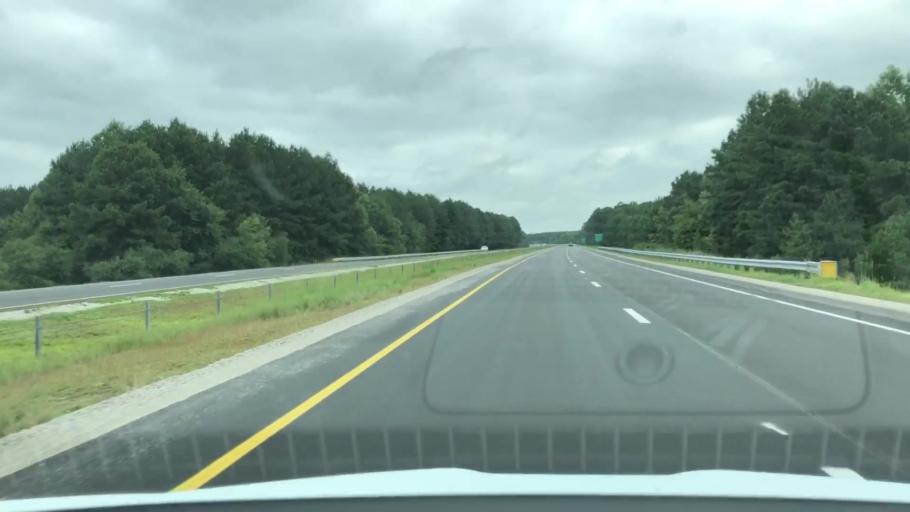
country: US
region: North Carolina
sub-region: Wilson County
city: Lucama
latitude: 35.6508
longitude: -77.9611
